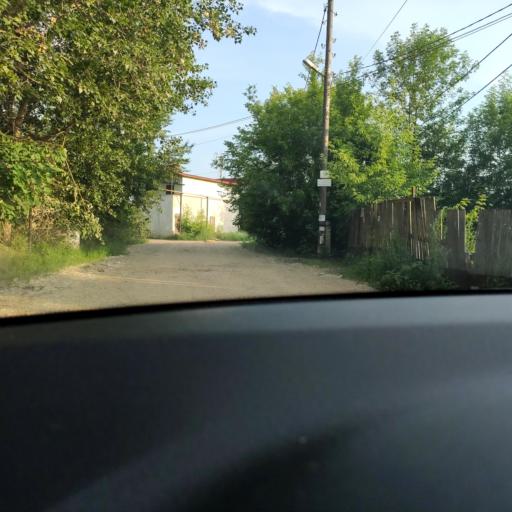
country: RU
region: Samara
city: Rozhdestveno
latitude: 53.1499
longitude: 50.0245
